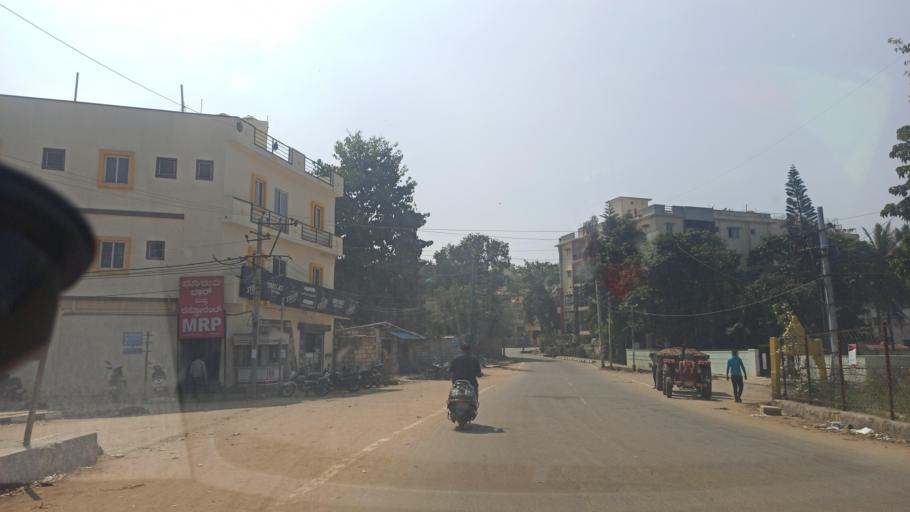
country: IN
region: Karnataka
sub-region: Bangalore Urban
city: Yelahanka
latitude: 13.0600
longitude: 77.6000
